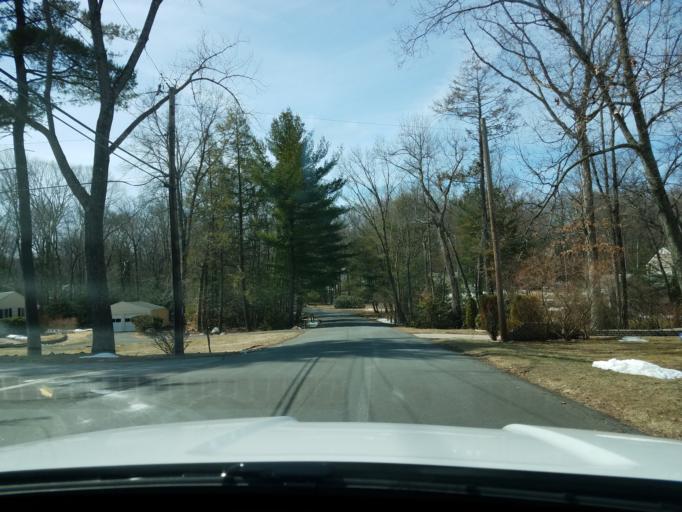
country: US
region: Connecticut
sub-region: Hartford County
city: Canton Valley
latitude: 41.7849
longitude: -72.8730
